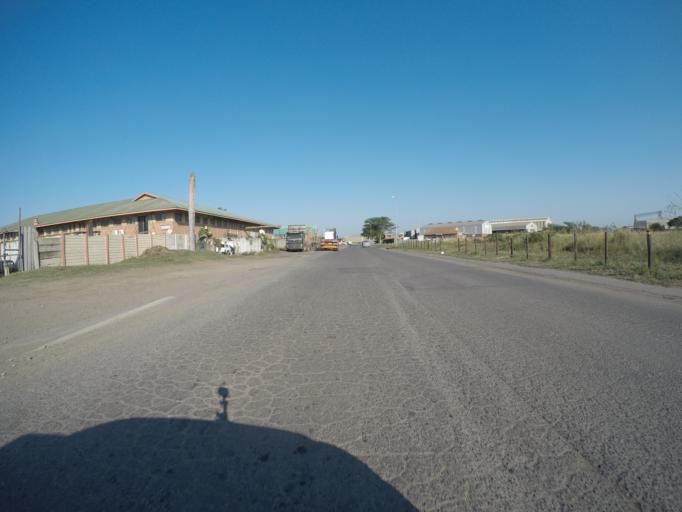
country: ZA
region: KwaZulu-Natal
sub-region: uThungulu District Municipality
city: Richards Bay
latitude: -28.7514
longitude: 32.0282
